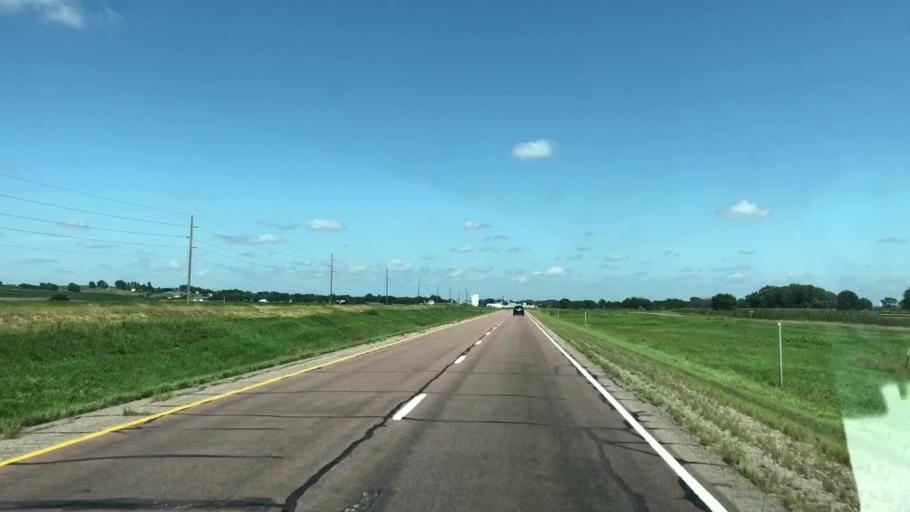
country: US
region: Iowa
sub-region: Plymouth County
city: Le Mars
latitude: 42.7007
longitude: -96.2575
